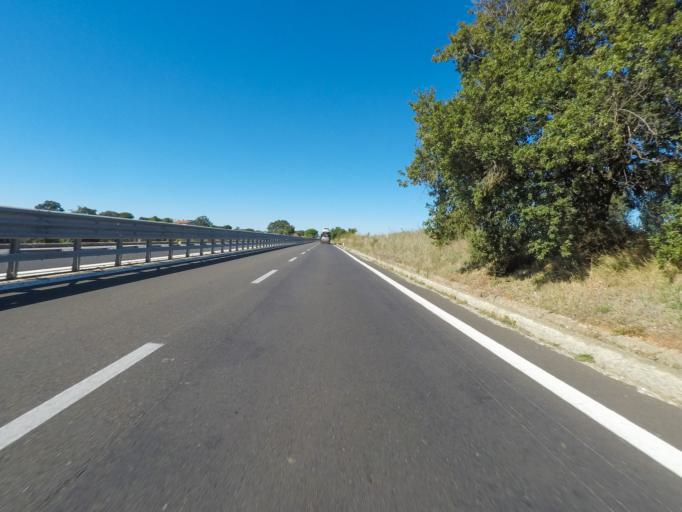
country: IT
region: Latium
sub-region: Provincia di Viterbo
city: Montalto di Castro
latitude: 42.3010
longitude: 11.6698
